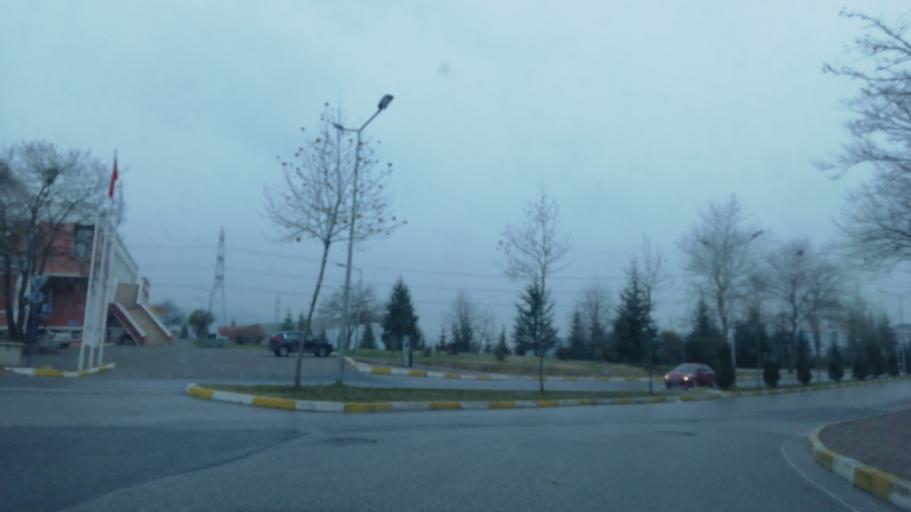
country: TR
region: Sakarya
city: Kazimpasa
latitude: 40.7427
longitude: 30.3377
